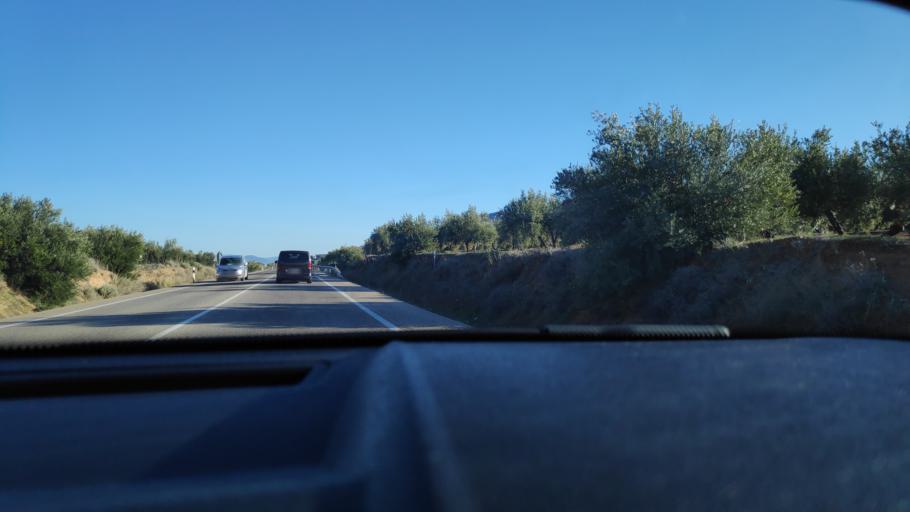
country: ES
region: Andalusia
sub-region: Province of Cordoba
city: Luque
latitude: 37.5678
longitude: -4.2331
